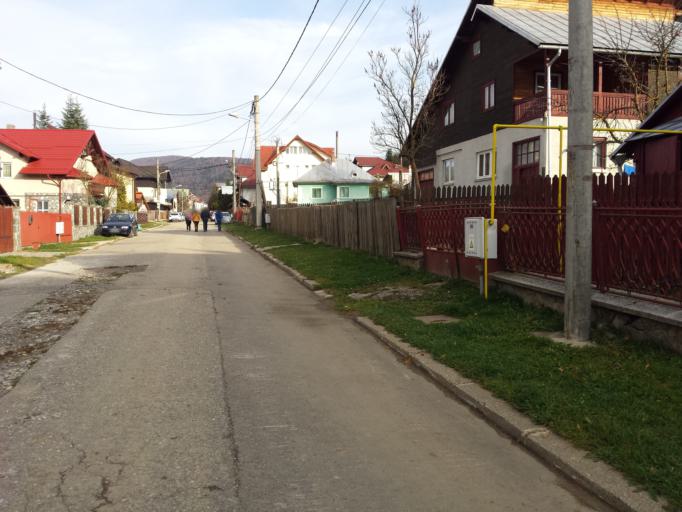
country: RO
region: Prahova
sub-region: Oras Busteni
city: Busteni
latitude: 45.4065
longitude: 25.5404
